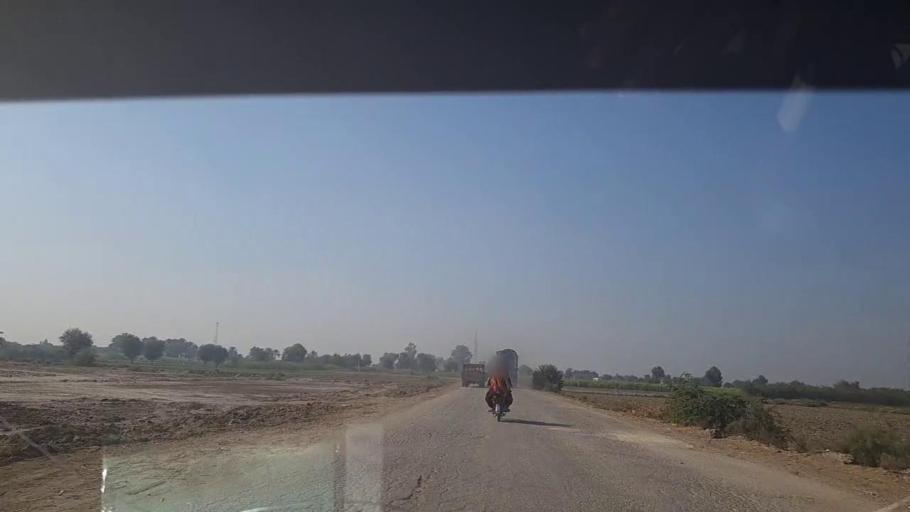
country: PK
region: Sindh
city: Kot Diji
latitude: 27.4365
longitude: 68.6395
